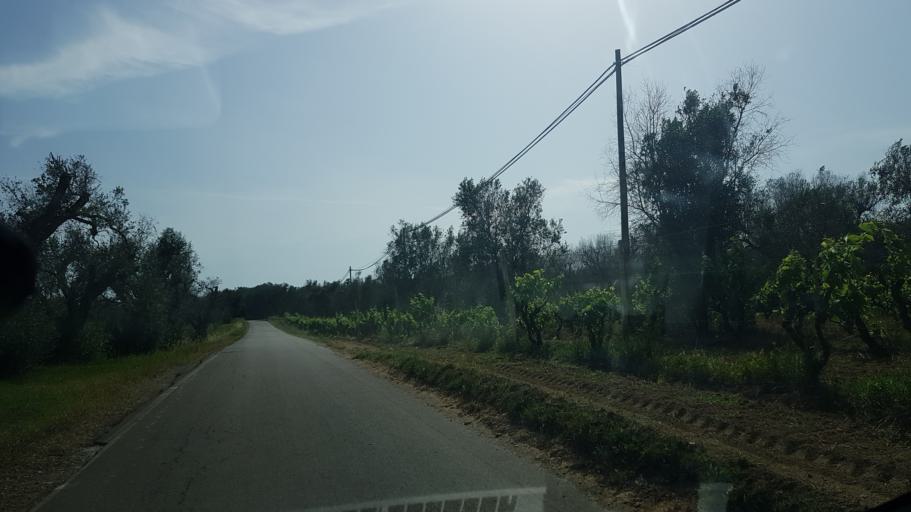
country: IT
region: Apulia
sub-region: Provincia di Brindisi
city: Torchiarolo
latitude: 40.5043
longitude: 18.0634
